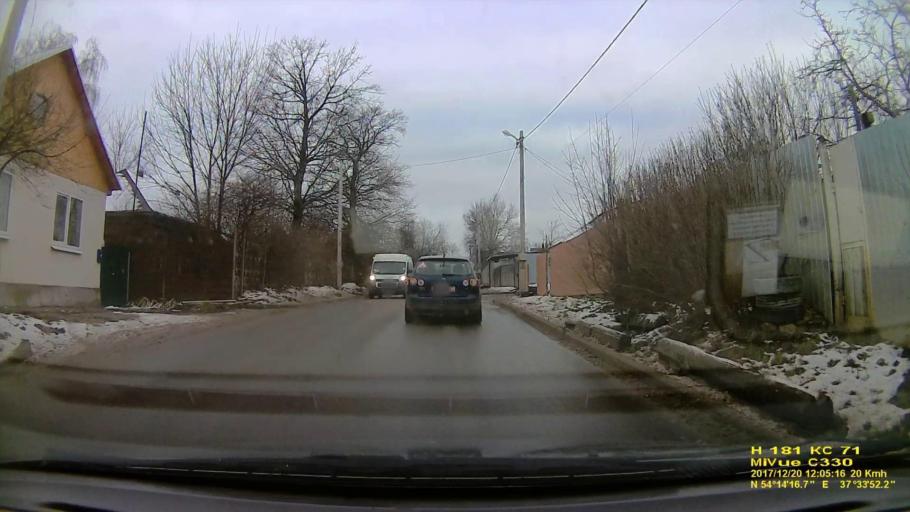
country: RU
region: Tula
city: Gorelki
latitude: 54.2381
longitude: 37.5644
